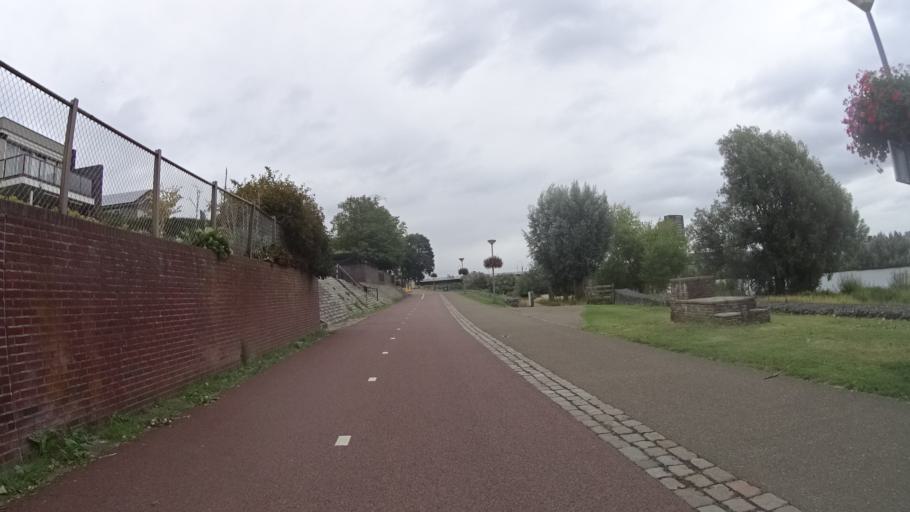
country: NL
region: Limburg
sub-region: Gemeente Venlo
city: Venlo
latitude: 51.3670
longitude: 6.1568
